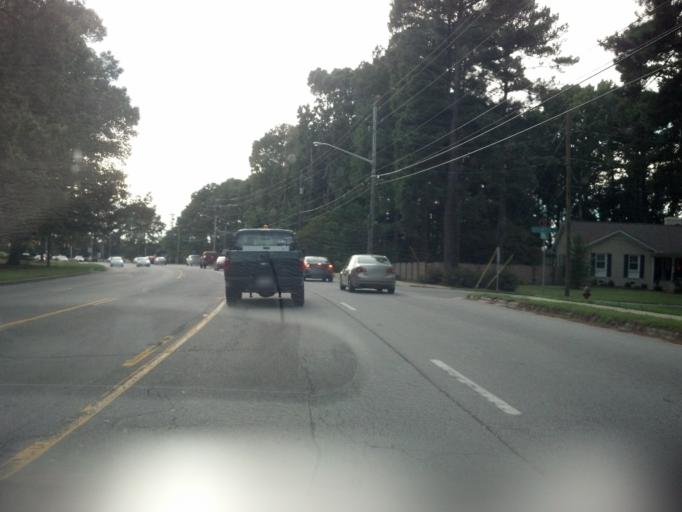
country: US
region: North Carolina
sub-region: Pitt County
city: Greenville
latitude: 35.5906
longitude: -77.3644
